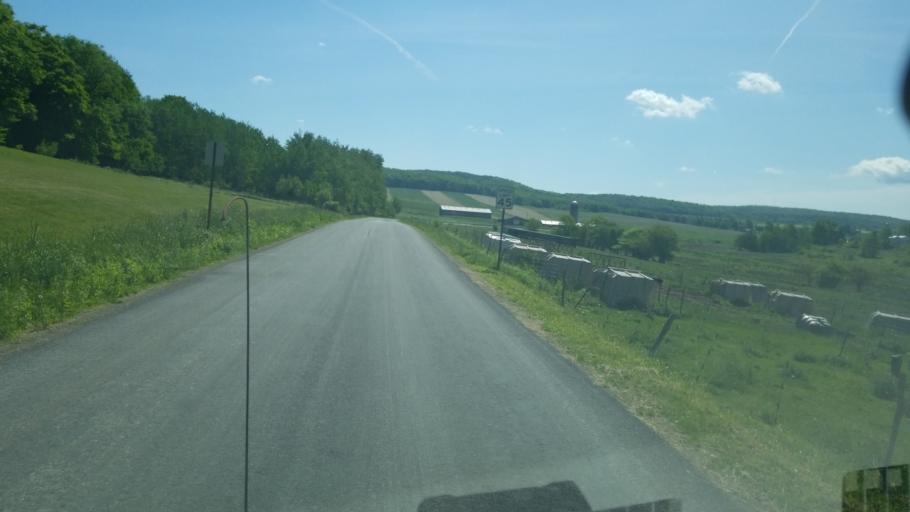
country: US
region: Pennsylvania
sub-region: Potter County
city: Galeton
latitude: 41.8954
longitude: -77.7520
